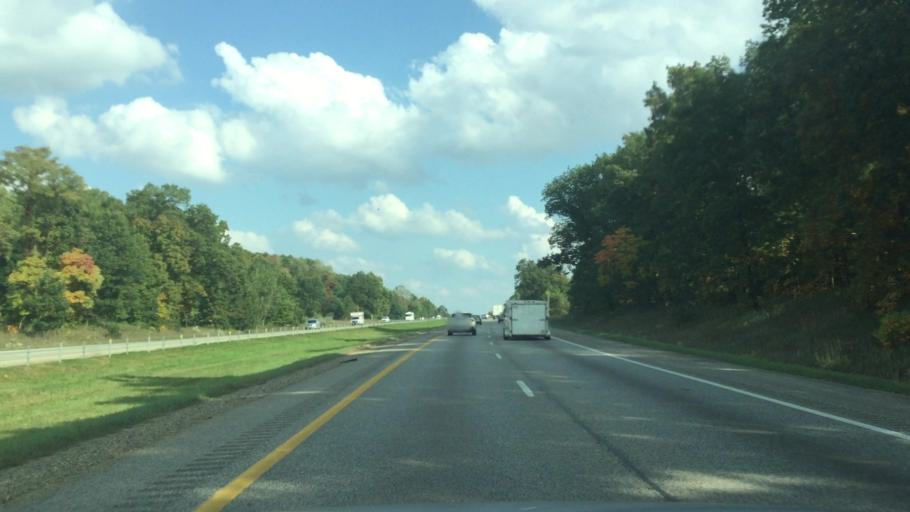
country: US
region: Michigan
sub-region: Kalamazoo County
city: Galesburg
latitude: 42.2820
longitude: -85.3463
